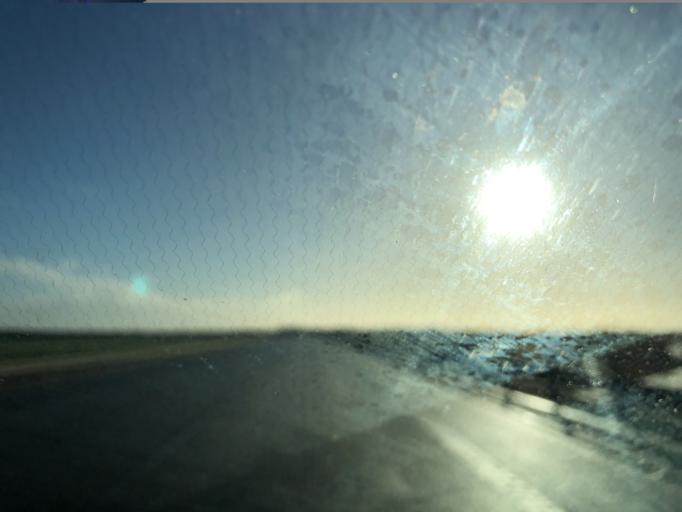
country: DK
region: Central Jutland
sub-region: Skive Kommune
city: Skive
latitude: 56.5442
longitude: 8.9973
